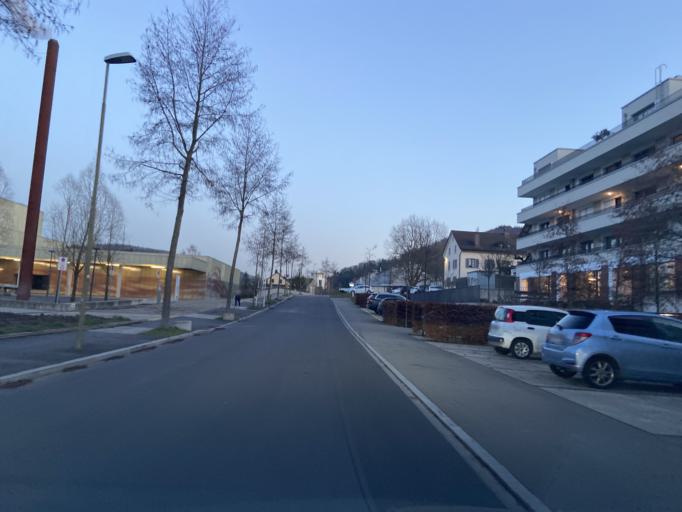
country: CH
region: Zurich
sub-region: Bezirk Winterthur
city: Wuelflingen (Kreis 6) / Niederfeld
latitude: 47.5074
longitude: 8.6805
